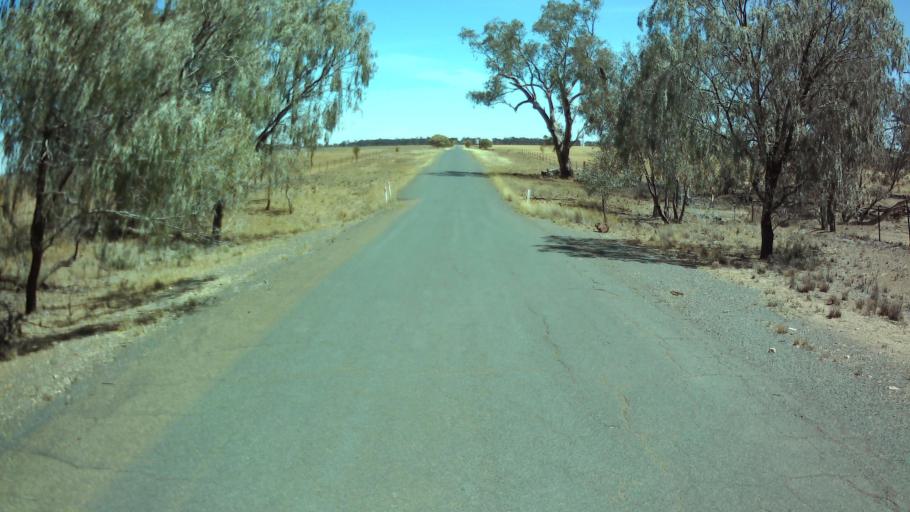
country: AU
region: New South Wales
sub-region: Weddin
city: Grenfell
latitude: -33.8492
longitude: 147.6959
